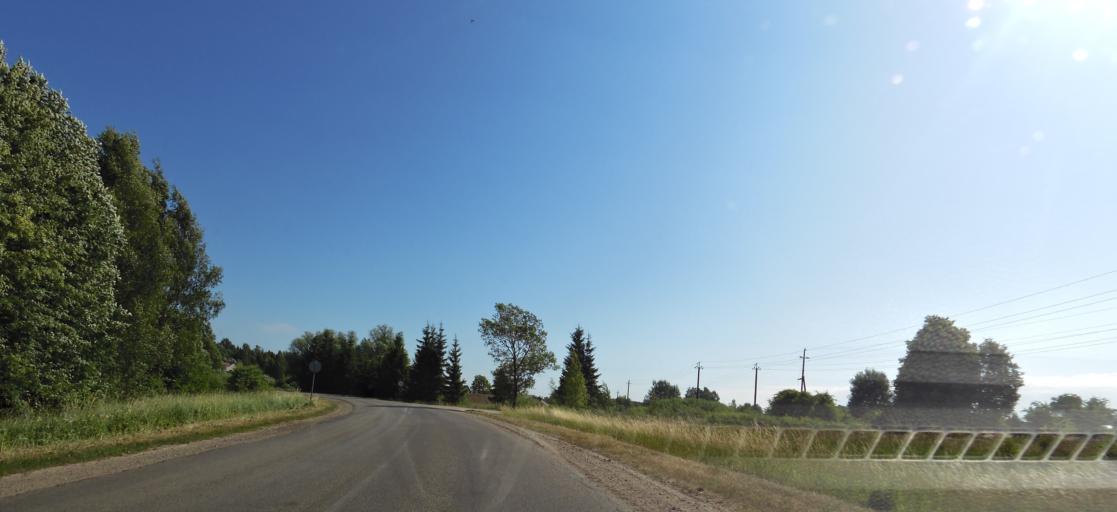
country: LT
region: Panevezys
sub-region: Birzai
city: Birzai
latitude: 56.2062
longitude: 24.7868
